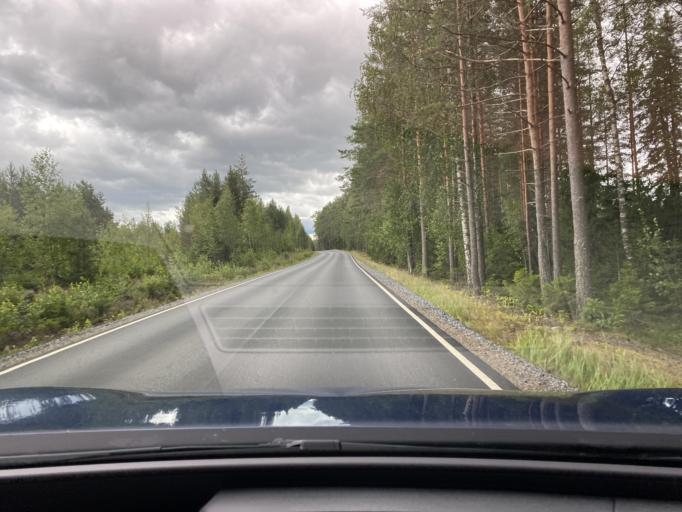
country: FI
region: Pirkanmaa
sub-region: Lounais-Pirkanmaa
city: Vammala
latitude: 61.2893
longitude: 23.0092
